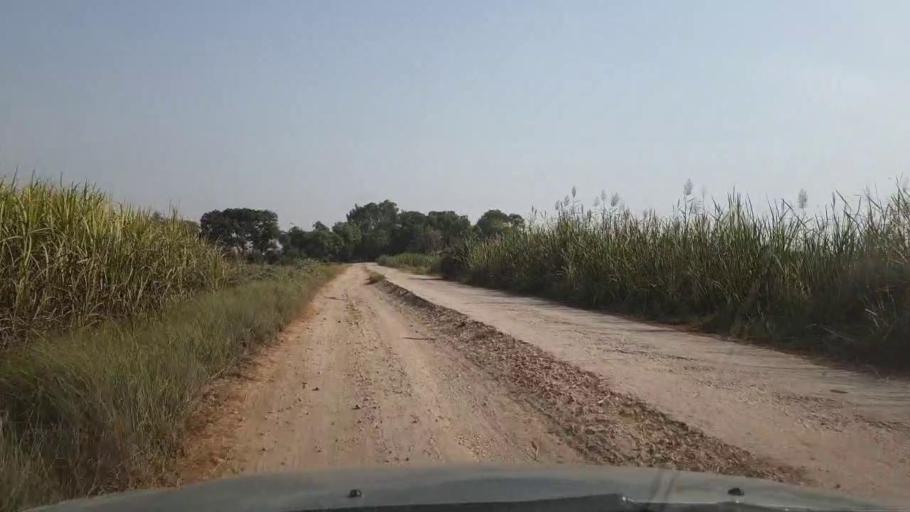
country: PK
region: Sindh
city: Bulri
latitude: 24.9068
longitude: 68.3734
